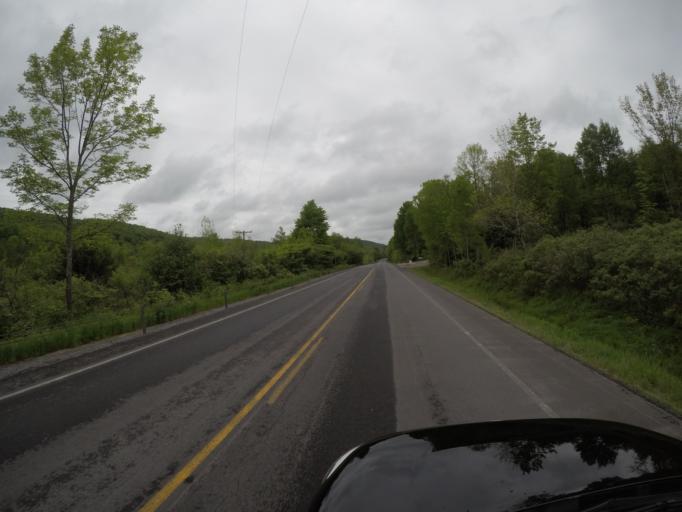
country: US
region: New York
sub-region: Delaware County
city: Delhi
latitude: 42.2088
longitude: -74.7918
